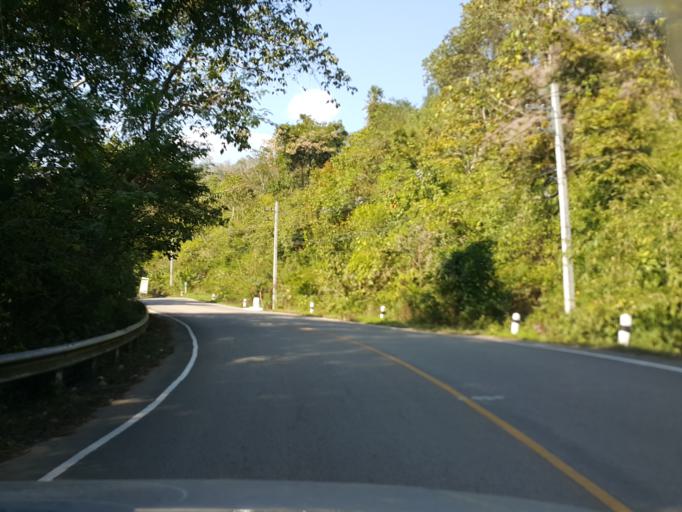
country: TH
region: Chiang Mai
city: Mae Wang
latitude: 18.6347
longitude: 98.7050
